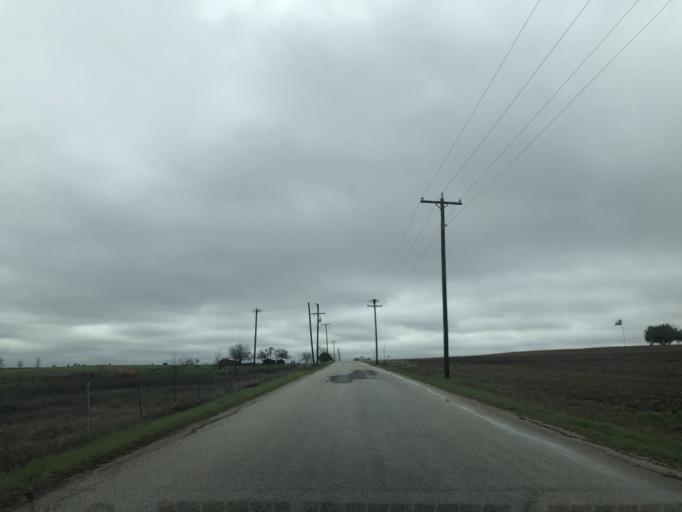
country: US
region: Texas
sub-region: Williamson County
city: Hutto
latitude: 30.5827
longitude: -97.4968
